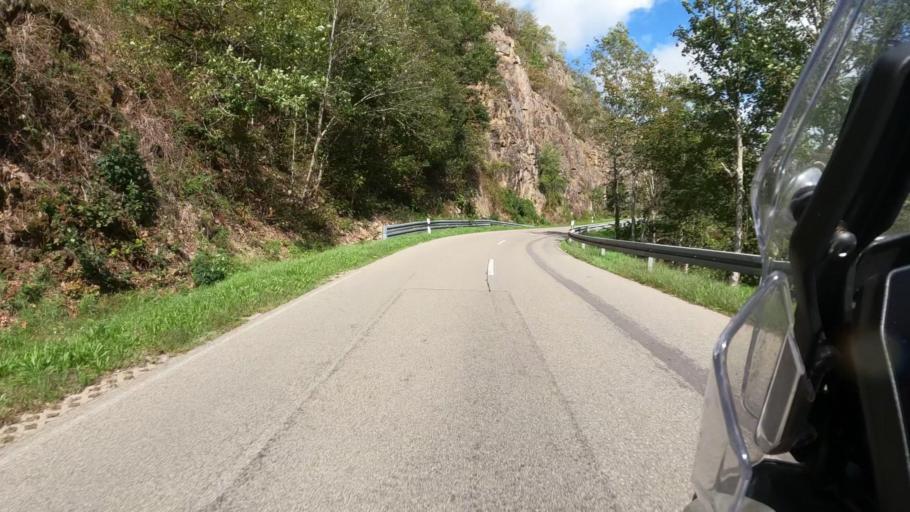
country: DE
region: Baden-Wuerttemberg
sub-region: Freiburg Region
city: Weilheim
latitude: 47.6829
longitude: 8.2577
